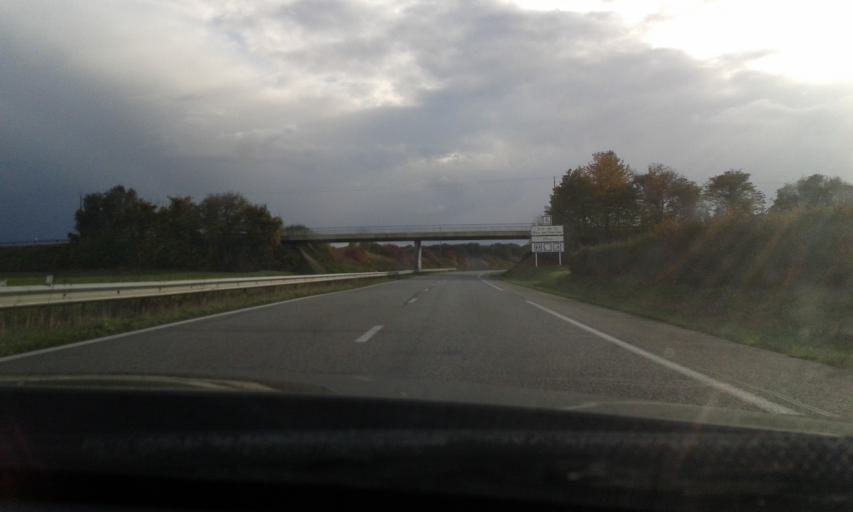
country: FR
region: Haute-Normandie
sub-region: Departement de l'Eure
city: Normanville
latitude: 49.0823
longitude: 1.1882
